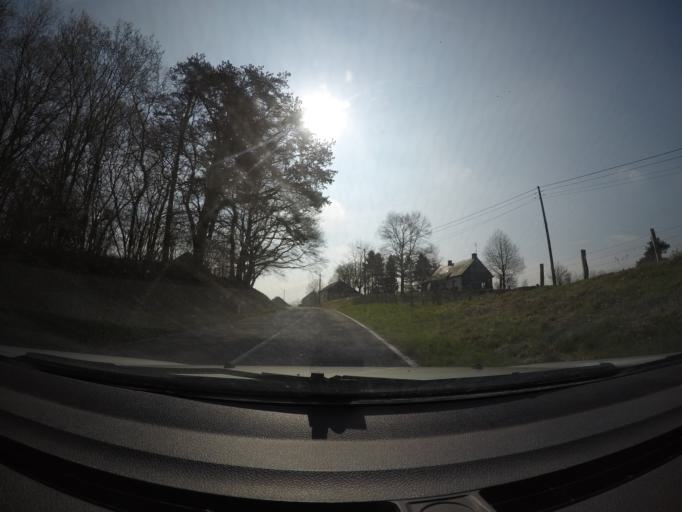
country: BE
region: Wallonia
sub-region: Province du Luxembourg
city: Tintigny
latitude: 49.7171
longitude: 5.5153
